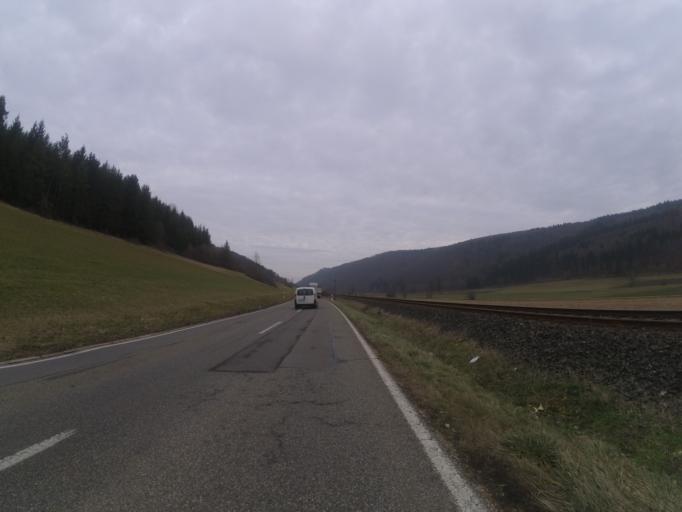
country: DE
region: Baden-Wuerttemberg
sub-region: Tuebingen Region
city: Schelklingen
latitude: 48.3669
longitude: 9.6625
